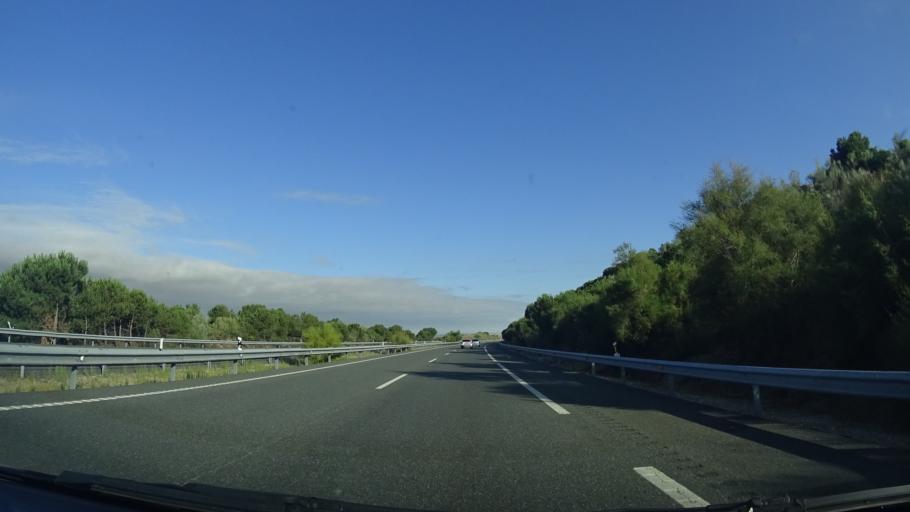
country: ES
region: Castille and Leon
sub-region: Provincia de Segovia
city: Labajos
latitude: 40.8397
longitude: -4.5350
